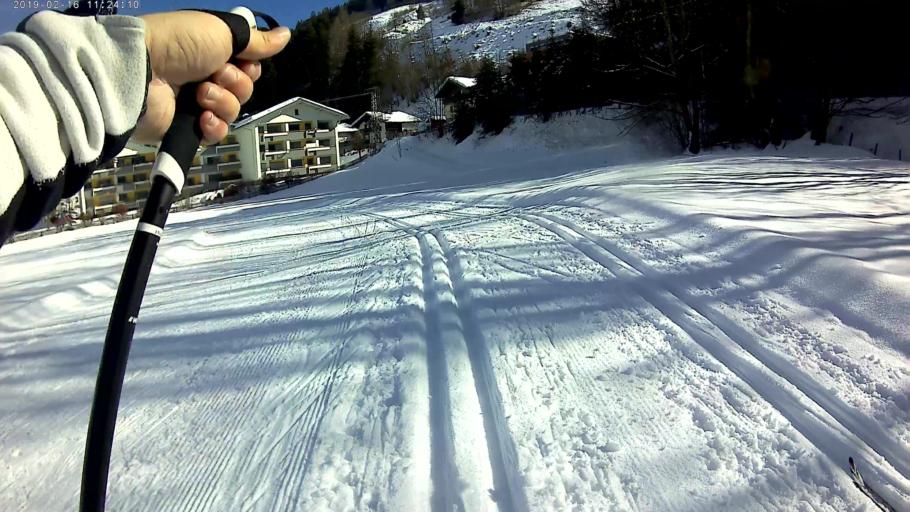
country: AT
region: Salzburg
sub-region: Politischer Bezirk Sankt Johann im Pongau
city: Sankt Johann im Pongau
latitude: 47.3316
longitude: 13.1942
